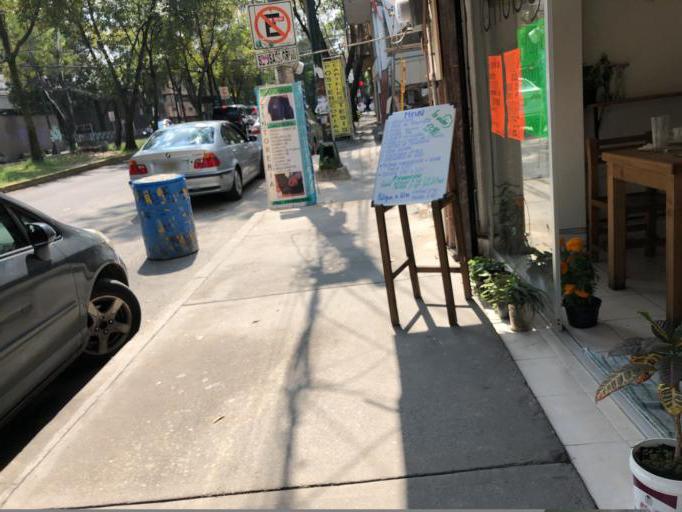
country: MX
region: Mexico City
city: Coyoacan
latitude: 19.3354
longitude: -99.1765
